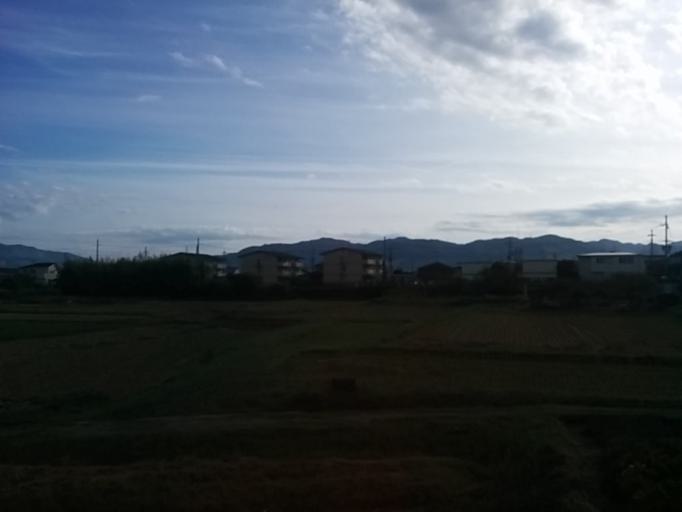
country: JP
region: Kyoto
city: Tanabe
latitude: 34.8098
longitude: 135.7774
